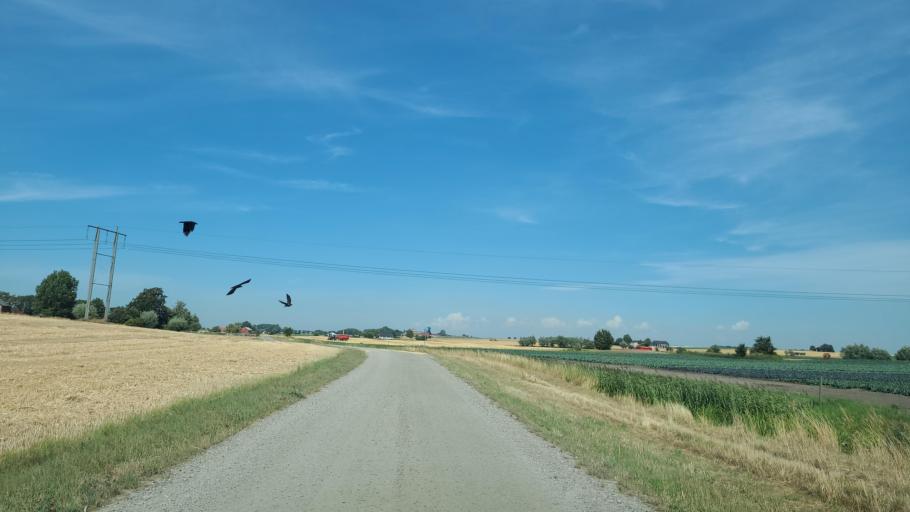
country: SE
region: Skane
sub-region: Trelleborgs Kommun
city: Skare
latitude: 55.4177
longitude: 13.0659
